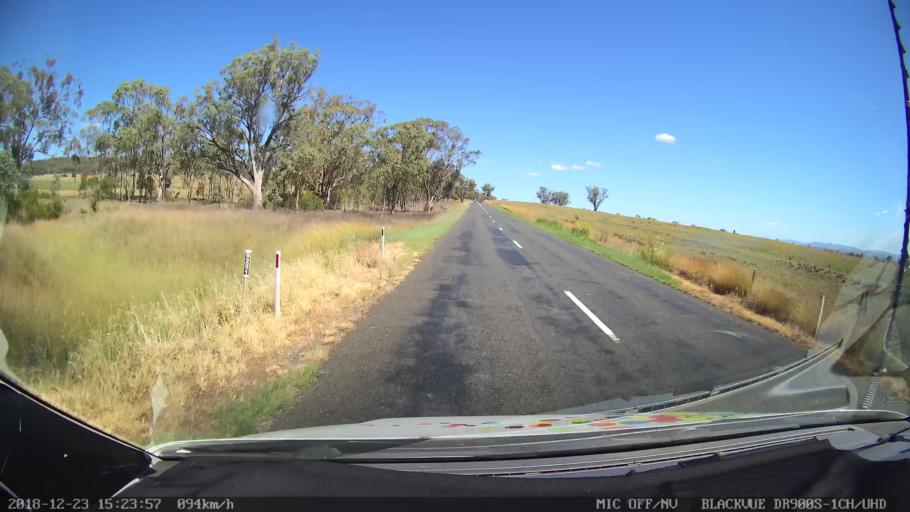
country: AU
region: New South Wales
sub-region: Tamworth Municipality
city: Manilla
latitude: -30.8862
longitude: 150.8191
